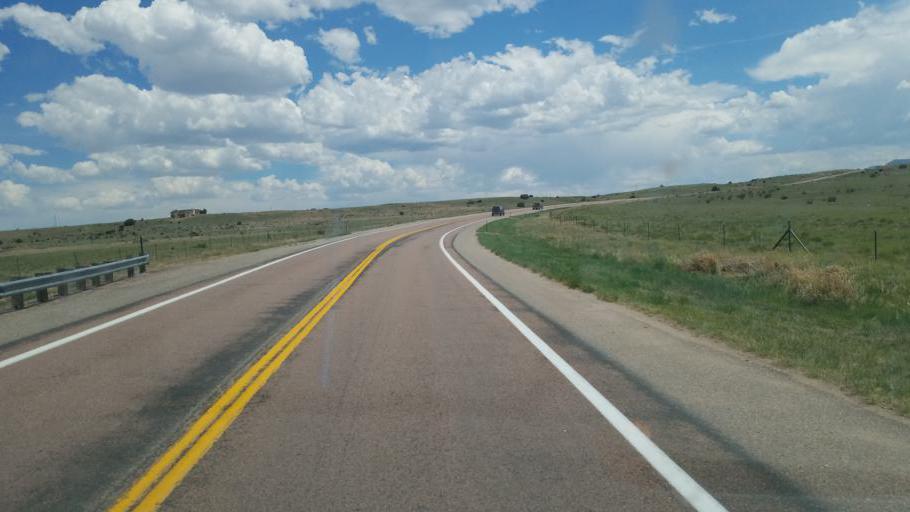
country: US
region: Colorado
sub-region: Fremont County
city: Florence
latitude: 38.2983
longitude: -105.0885
